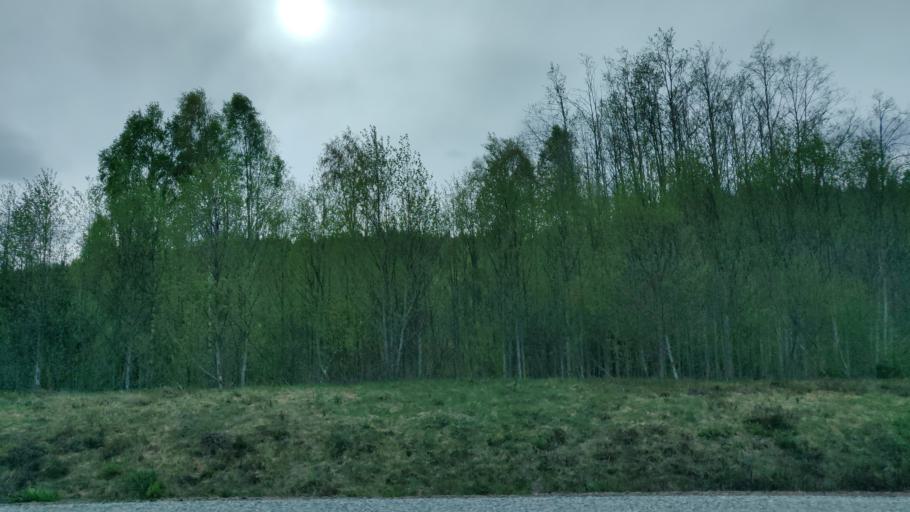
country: SE
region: Vaermland
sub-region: Munkfors Kommun
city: Munkfors
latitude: 59.7469
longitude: 13.4388
